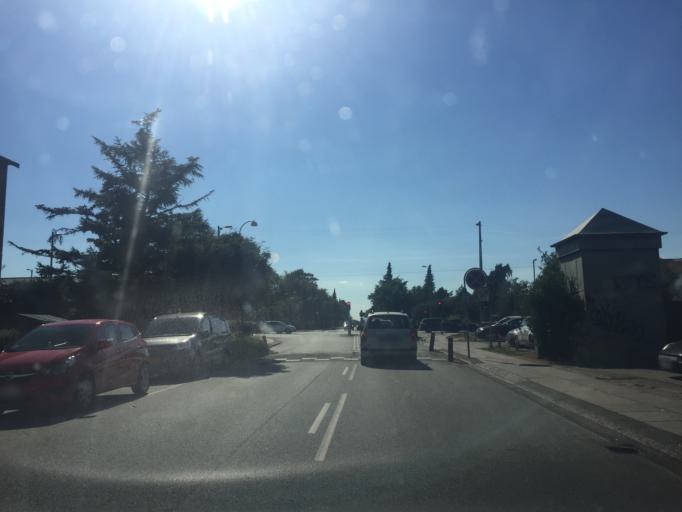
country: DK
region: Capital Region
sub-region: Gladsaxe Municipality
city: Buddinge
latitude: 55.7568
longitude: 12.4963
